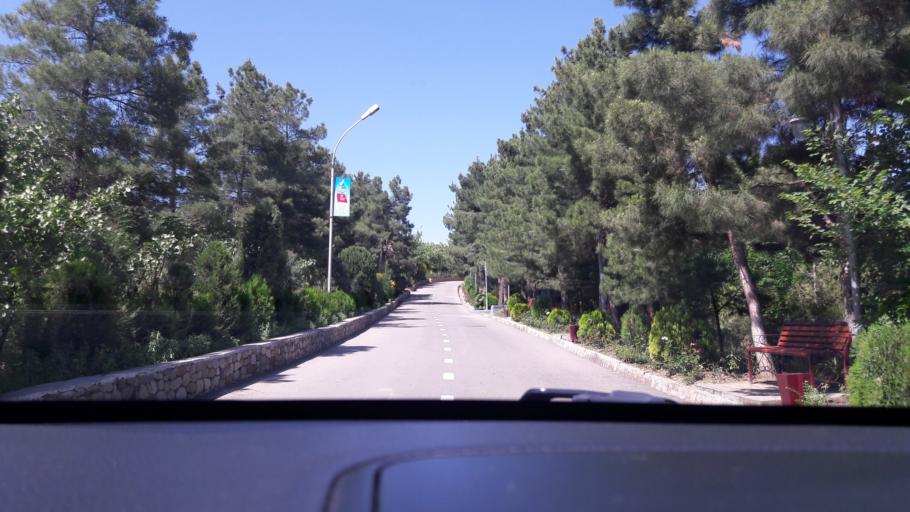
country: TJ
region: Dushanbe
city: Dushanbe
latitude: 38.5811
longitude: 68.8121
